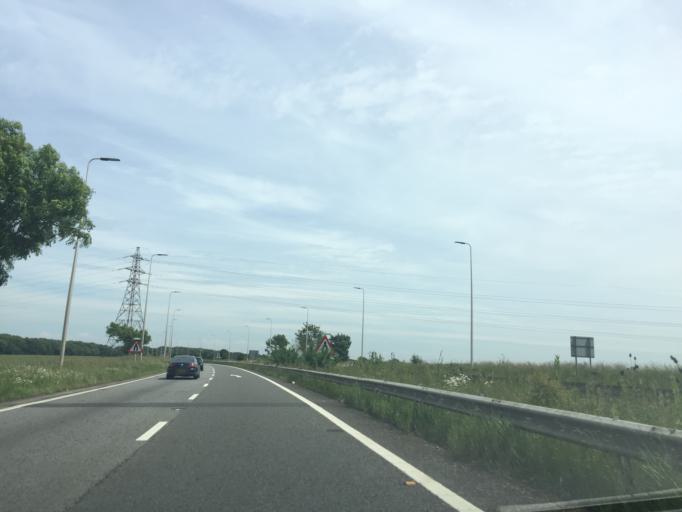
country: GB
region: England
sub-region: Kent
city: Shepherdswell
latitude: 51.1744
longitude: 1.2180
